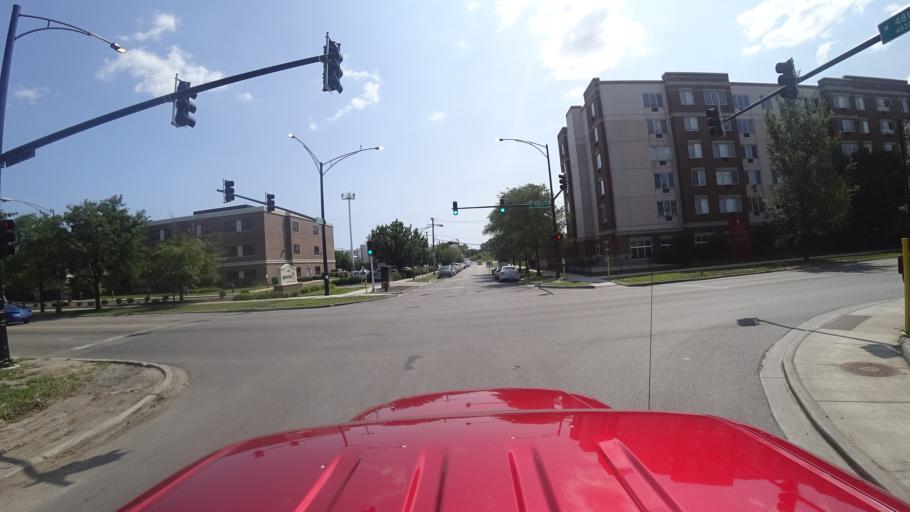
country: US
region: Illinois
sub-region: Cook County
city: Chicago
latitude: 41.8057
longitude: -87.6840
